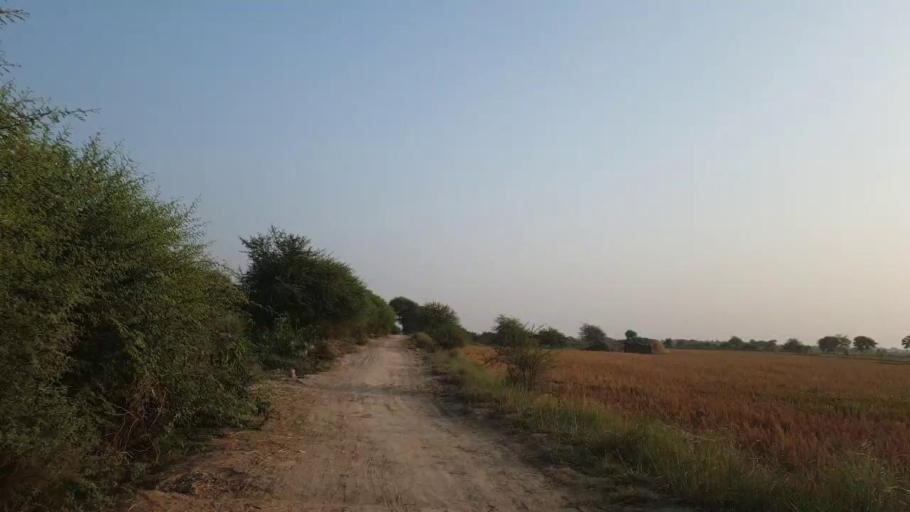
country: PK
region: Sindh
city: Kario
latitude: 24.8568
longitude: 68.6271
